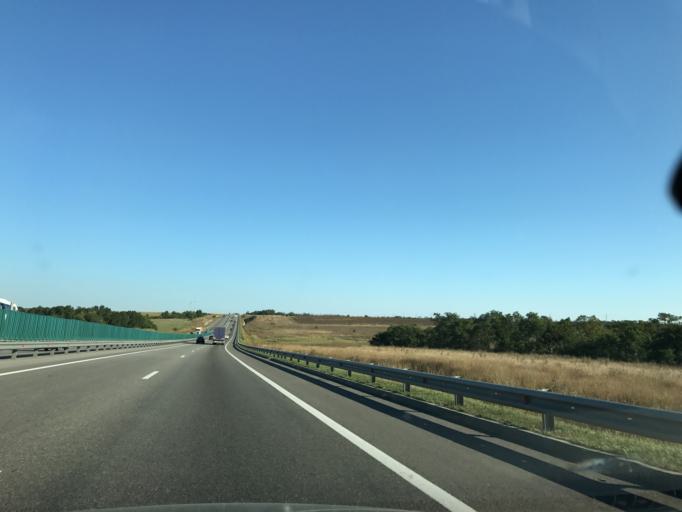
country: RU
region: Rostov
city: Glubokiy
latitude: 48.6022
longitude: 40.3540
